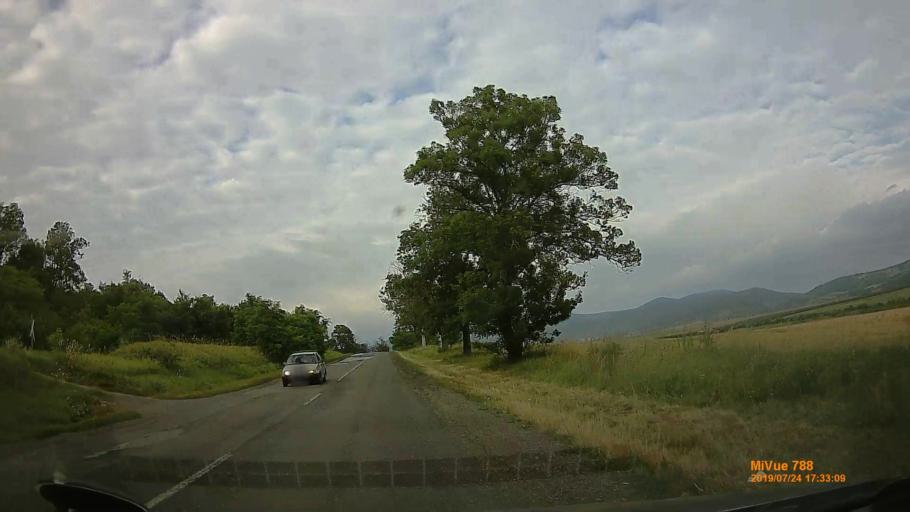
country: HU
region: Borsod-Abauj-Zemplen
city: Abaujszanto
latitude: 48.2909
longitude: 21.1877
